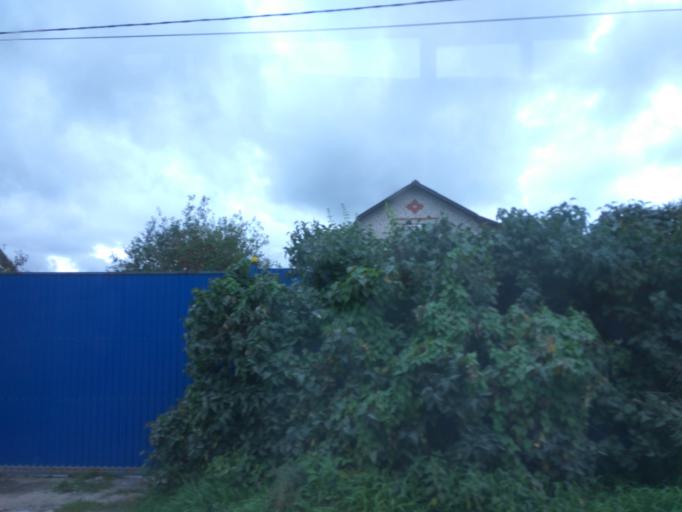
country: RU
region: Moskovskaya
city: Malyshevo
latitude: 55.5087
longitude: 38.3449
